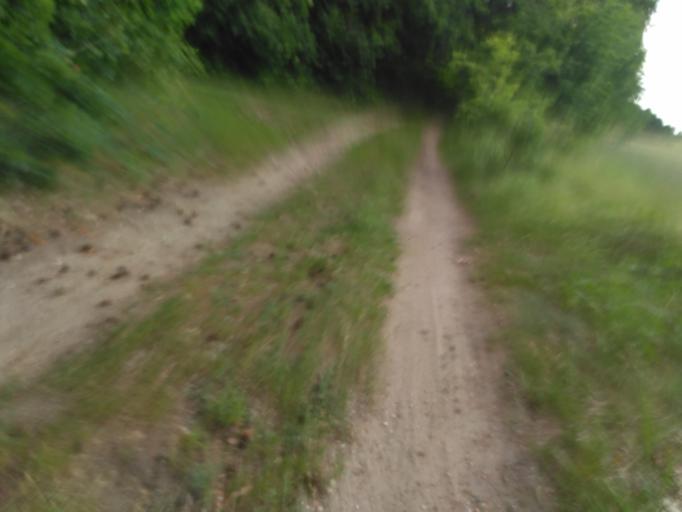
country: DE
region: Brandenburg
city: Elsterwerda
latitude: 51.4864
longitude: 13.5241
